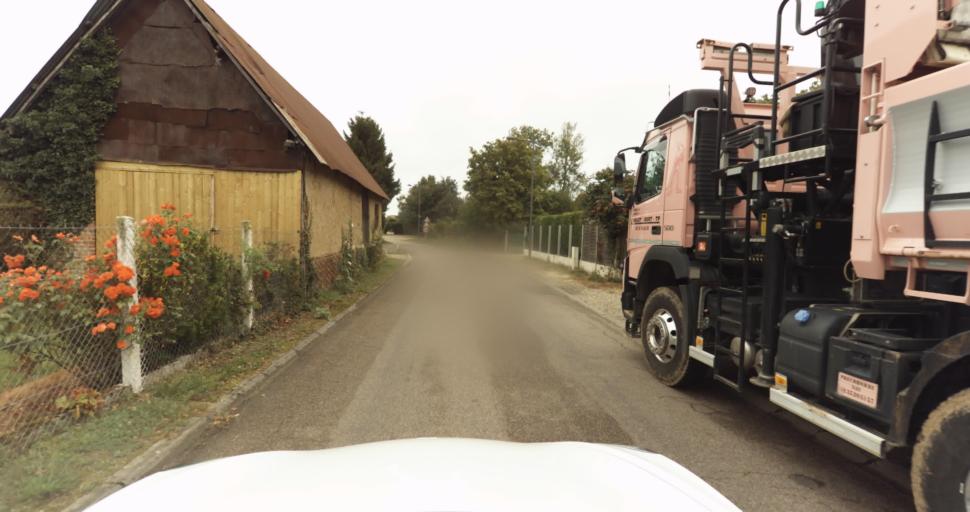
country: FR
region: Haute-Normandie
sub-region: Departement de l'Eure
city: Aviron
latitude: 49.0669
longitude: 1.0714
